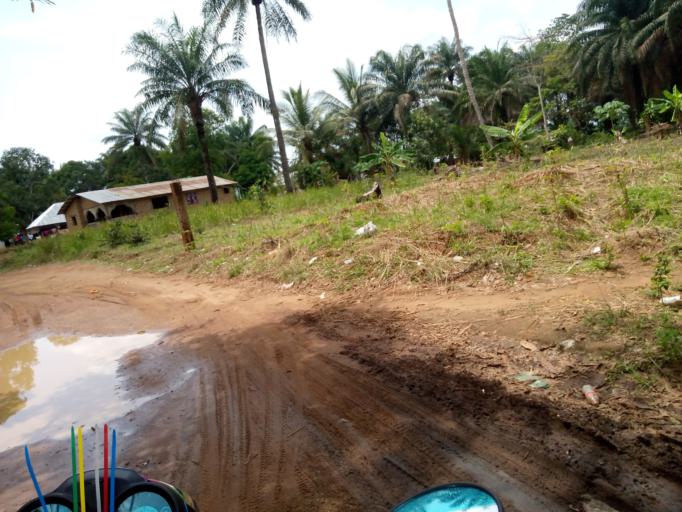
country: SL
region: Western Area
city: Waterloo
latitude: 8.3394
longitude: -13.0084
